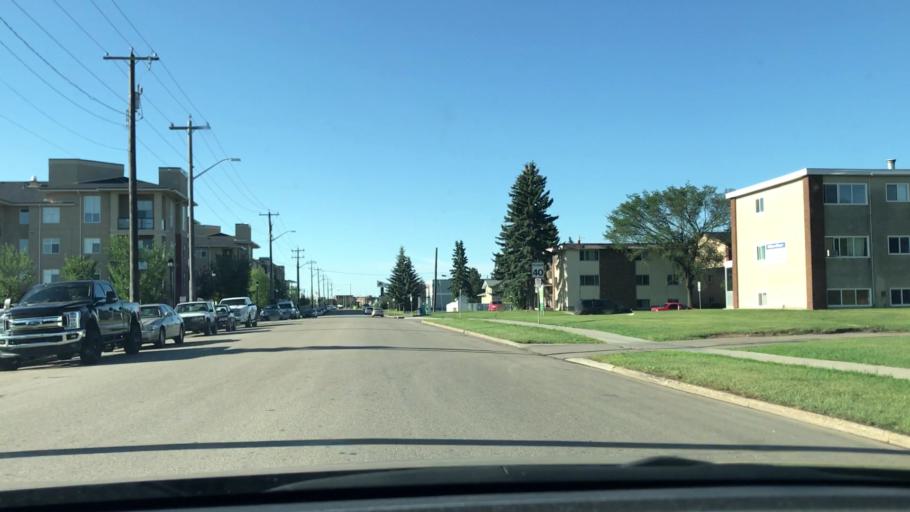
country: CA
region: Alberta
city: Edmonton
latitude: 53.5168
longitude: -113.4368
